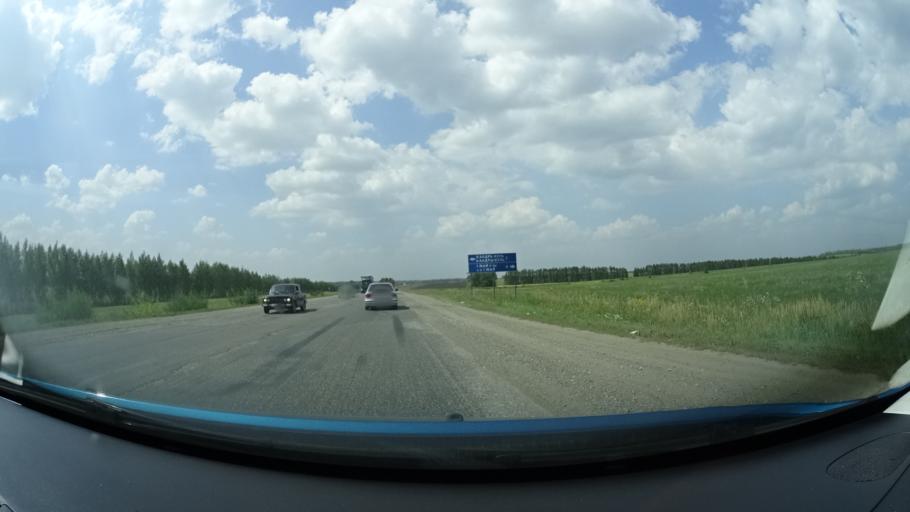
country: RU
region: Bashkortostan
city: Kandry
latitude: 54.5140
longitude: 53.9931
